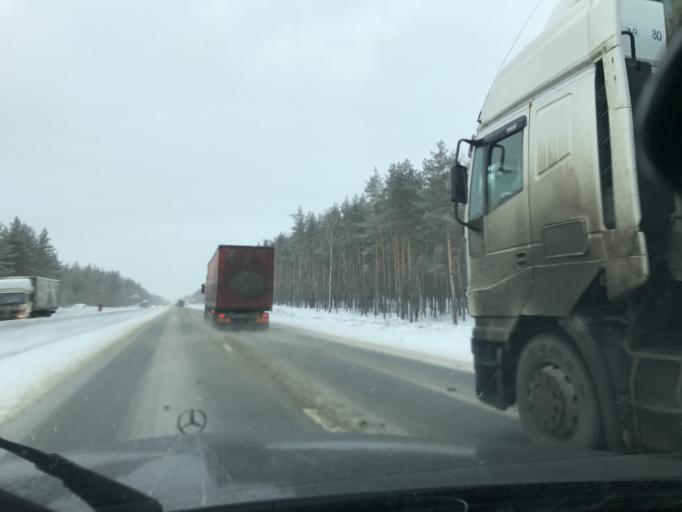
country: RU
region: Nizjnij Novgorod
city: Pyra
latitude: 56.2952
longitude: 43.3982
